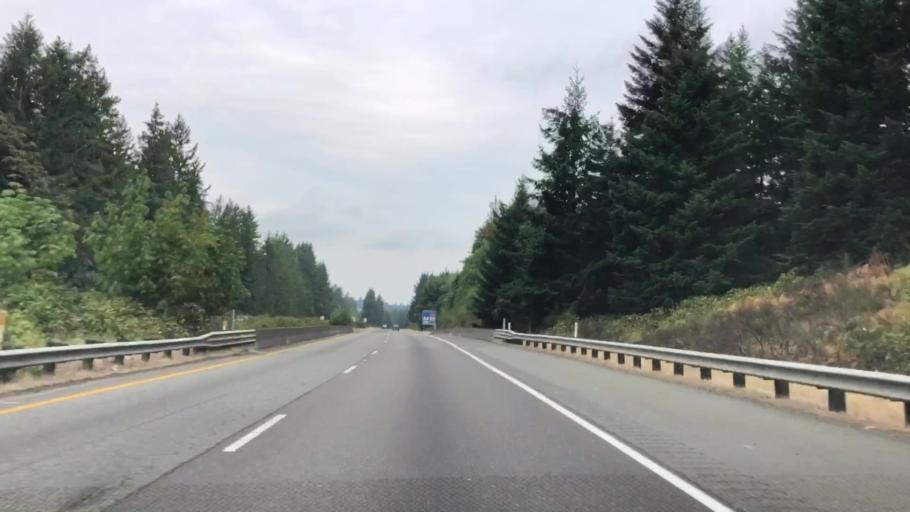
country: US
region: Washington
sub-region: Kitsap County
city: Bethel
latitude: 47.5113
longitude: -122.6520
